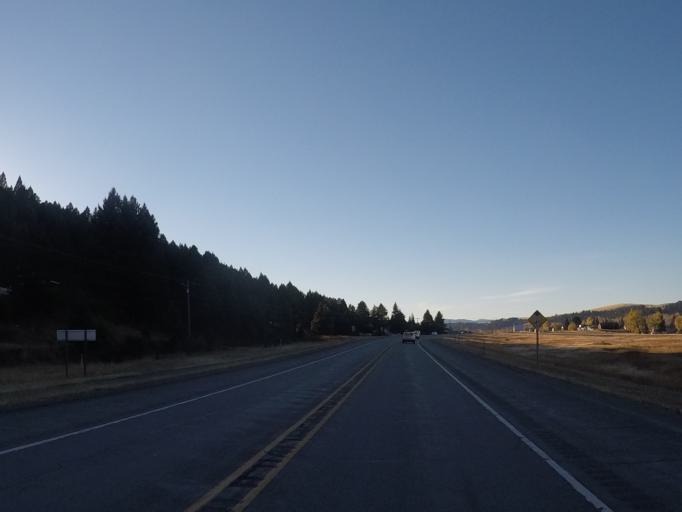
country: US
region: Montana
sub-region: Lewis and Clark County
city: Helena West Side
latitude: 46.5588
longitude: -112.4234
